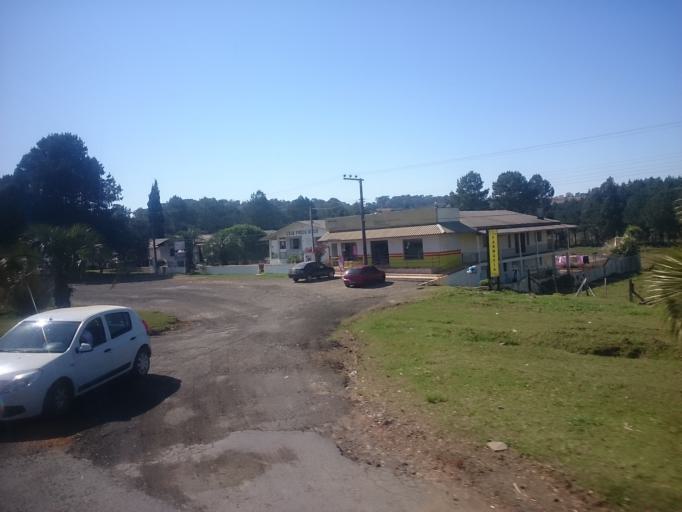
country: BR
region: Santa Catarina
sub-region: Curitibanos
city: Curitibanos
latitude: -27.1600
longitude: -50.4663
